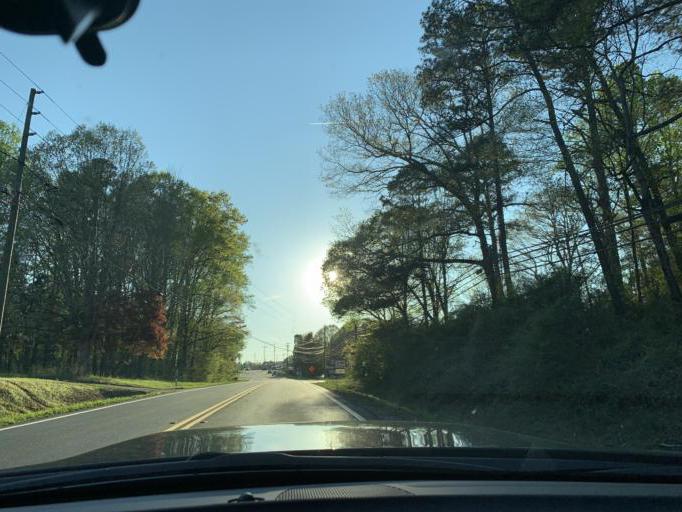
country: US
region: Georgia
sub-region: Forsyth County
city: Cumming
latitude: 34.2401
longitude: -84.1895
